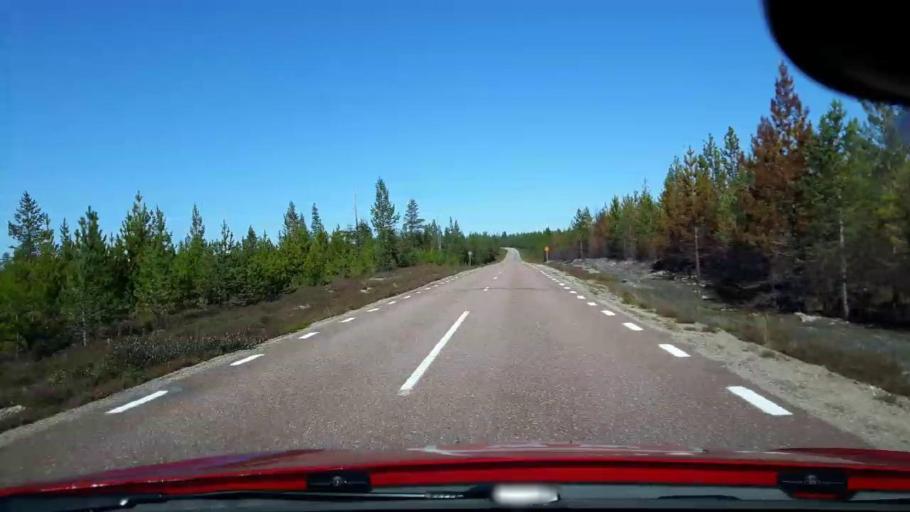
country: SE
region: Jaemtland
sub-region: Harjedalens Kommun
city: Sveg
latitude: 61.7141
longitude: 14.1686
